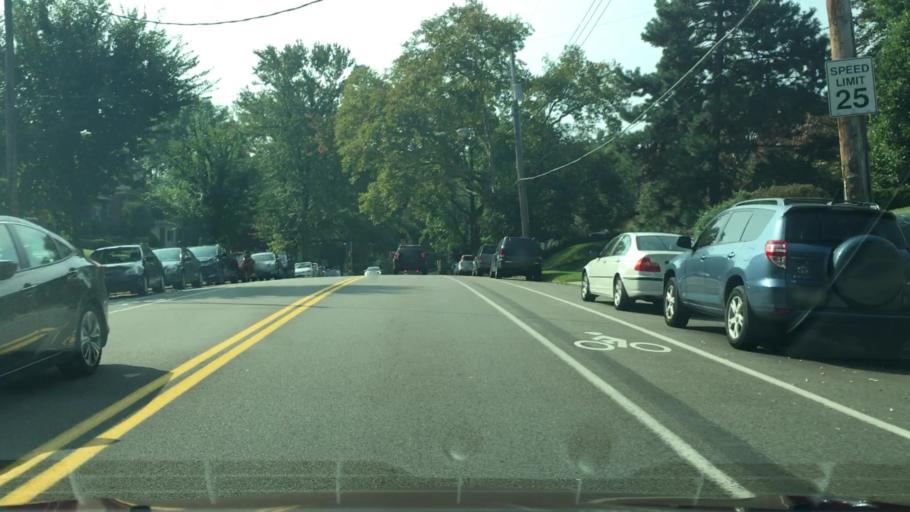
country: US
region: Pennsylvania
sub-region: Allegheny County
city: Homestead
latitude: 40.4394
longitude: -79.9165
